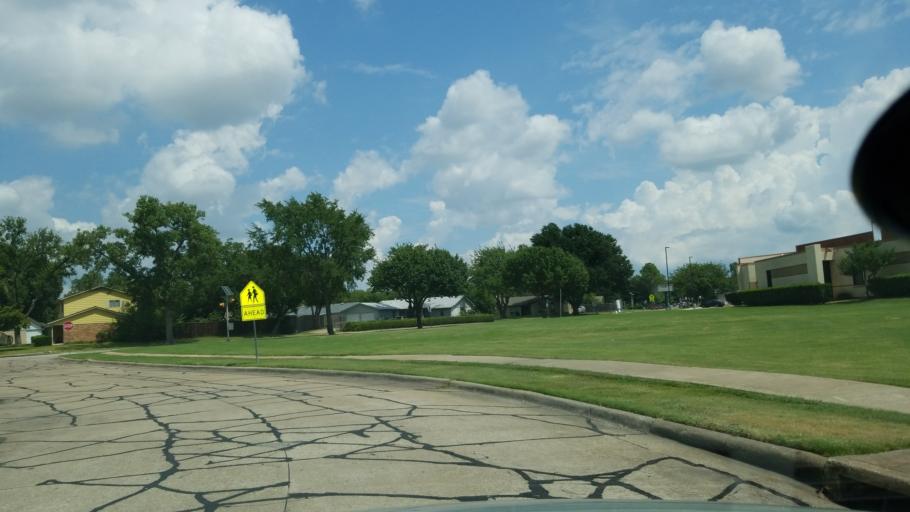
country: US
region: Texas
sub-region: Dallas County
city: Garland
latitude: 32.9242
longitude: -96.6554
